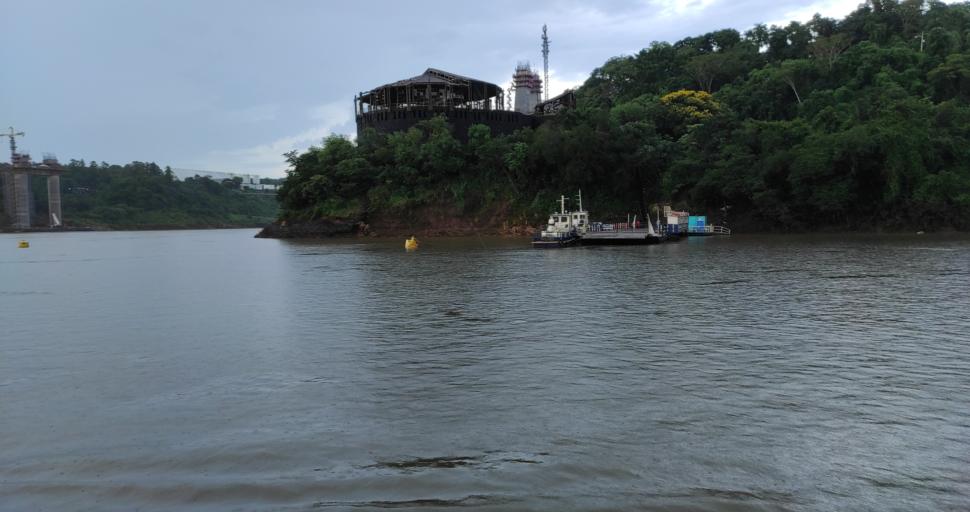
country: AR
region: Misiones
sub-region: Departamento de Iguazu
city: Puerto Iguazu
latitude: -25.5927
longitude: -54.5898
